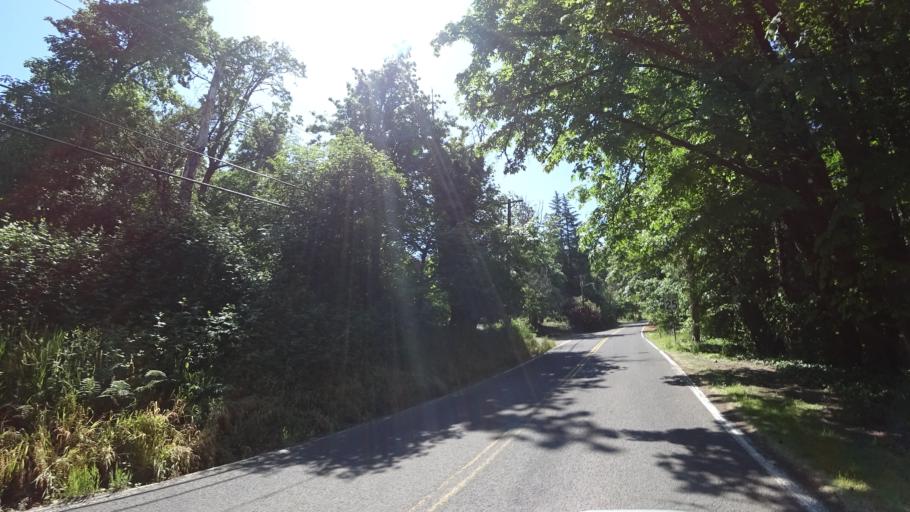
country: US
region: Oregon
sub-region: Clackamas County
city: Happy Valley
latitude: 45.4690
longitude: -122.5242
